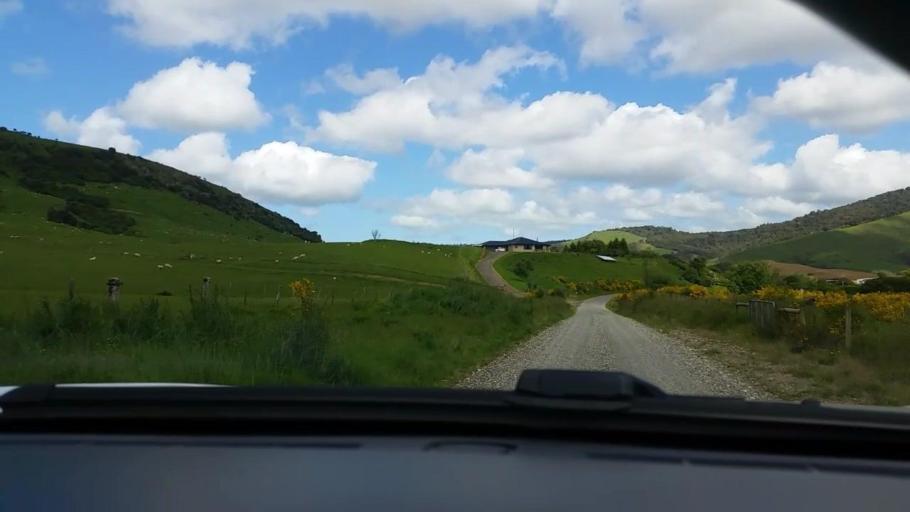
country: NZ
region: Otago
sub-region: Clutha District
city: Papatowai
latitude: -46.5902
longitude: 169.1481
